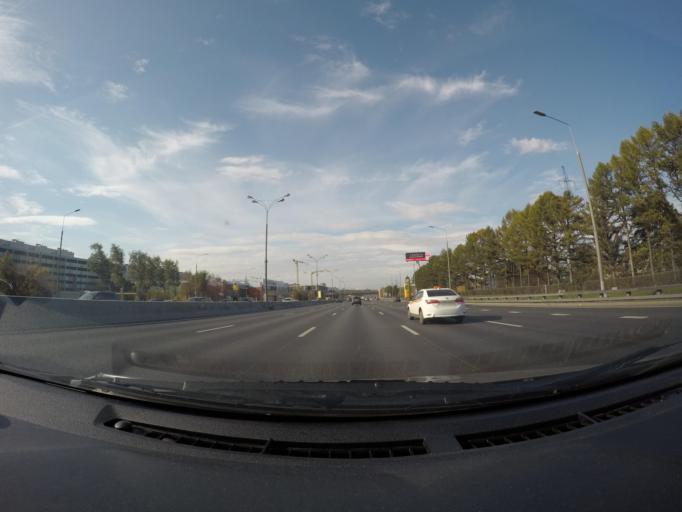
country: RU
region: Moscow
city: Kozeyevo
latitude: 55.8990
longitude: 37.6331
